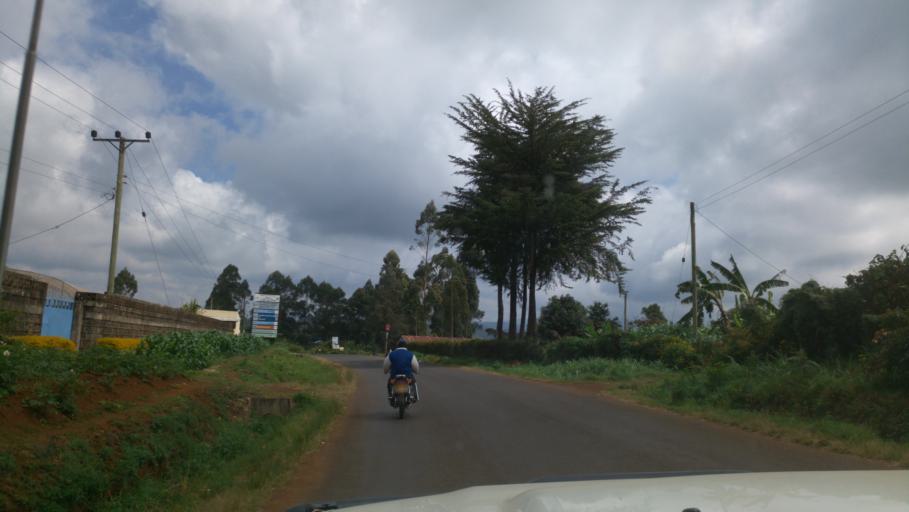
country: KE
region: Murang'a District
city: Kangema
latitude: -0.7717
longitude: 36.8413
